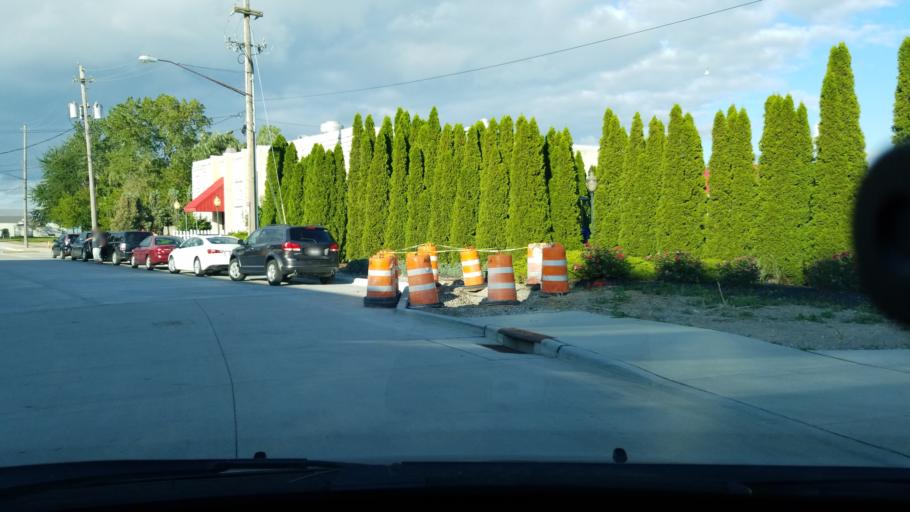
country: US
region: Ohio
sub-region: Erie County
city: Huron
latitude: 41.3957
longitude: -82.5531
